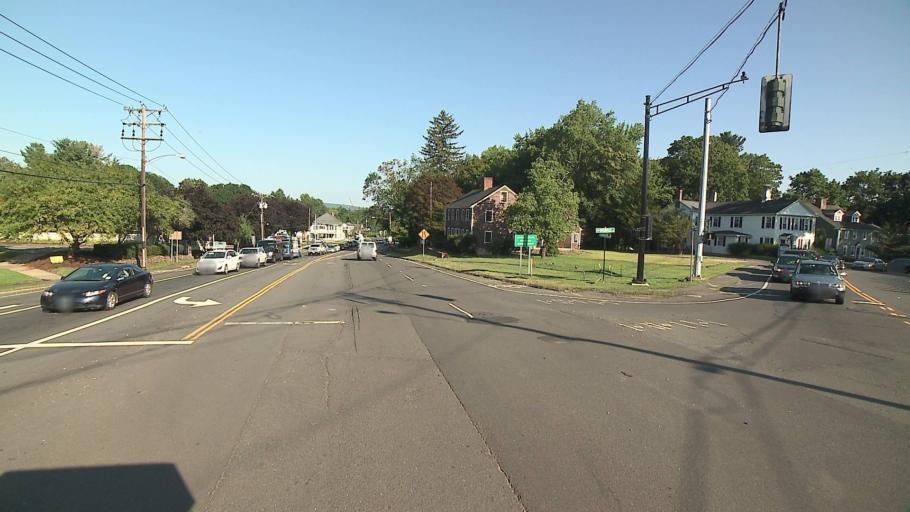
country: US
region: Connecticut
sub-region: Hartford County
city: Farmington
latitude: 41.7266
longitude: -72.8251
